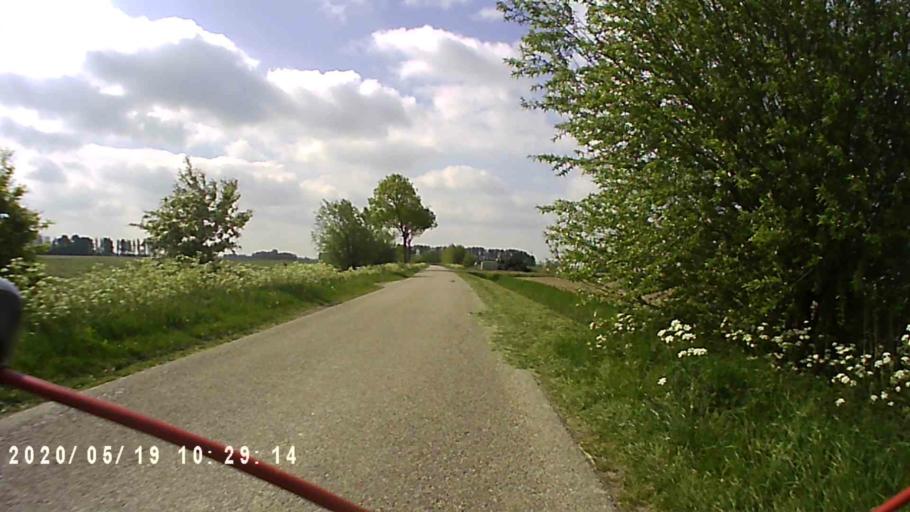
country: NL
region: Friesland
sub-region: Gemeente Kollumerland en Nieuwkruisland
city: Kollum
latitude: 53.2994
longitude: 6.1962
